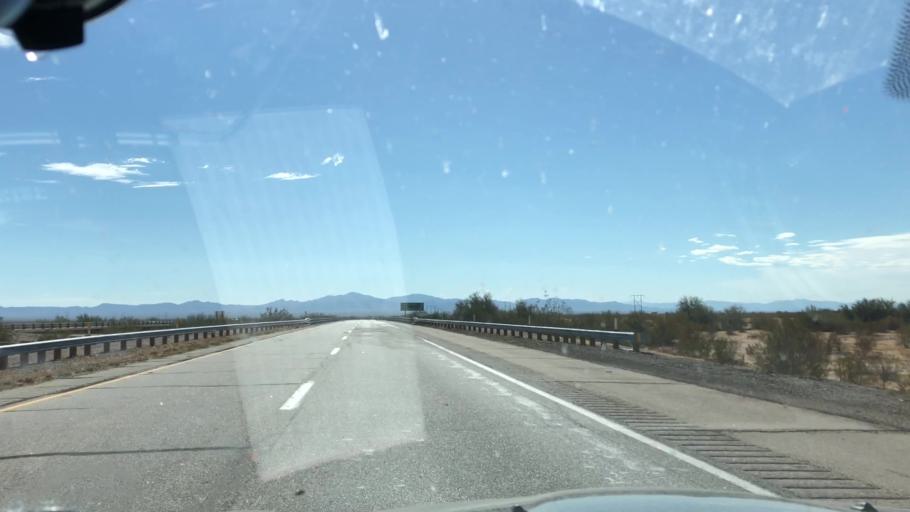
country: US
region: California
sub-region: Riverside County
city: Mesa Verde
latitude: 33.6069
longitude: -114.9177
